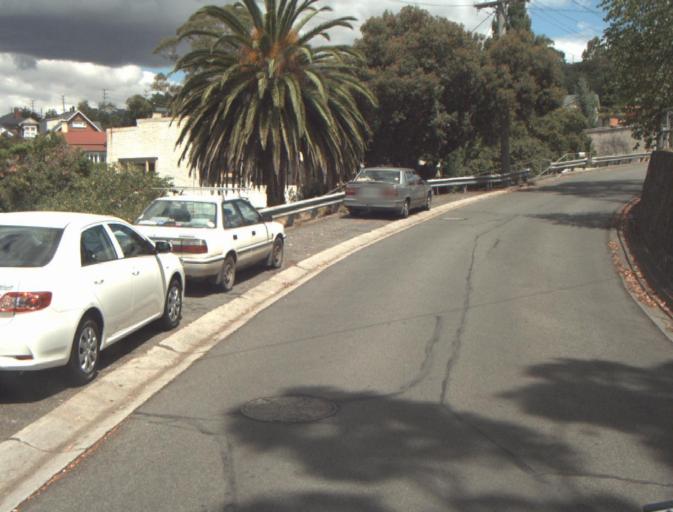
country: AU
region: Tasmania
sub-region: Launceston
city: Launceston
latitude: -41.4341
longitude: 147.1202
